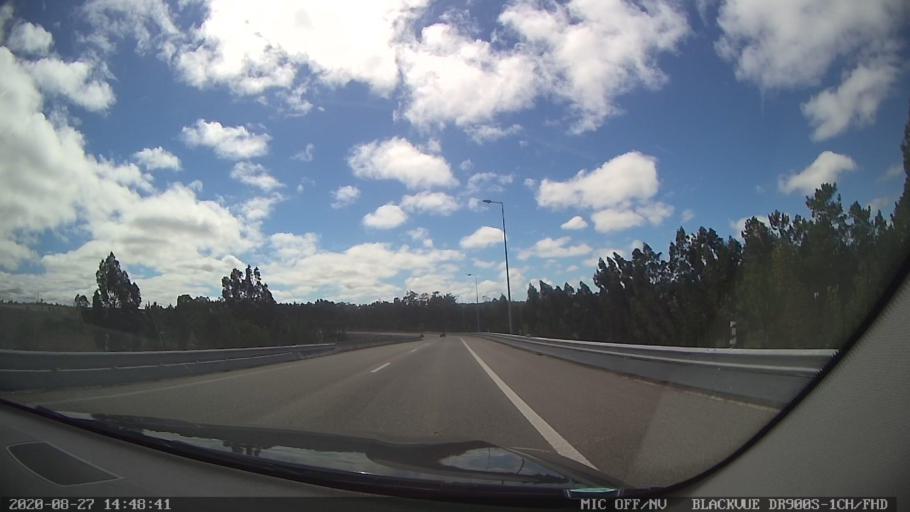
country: PT
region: Leiria
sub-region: Marinha Grande
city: Marinha Grande
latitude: 39.7437
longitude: -8.8847
